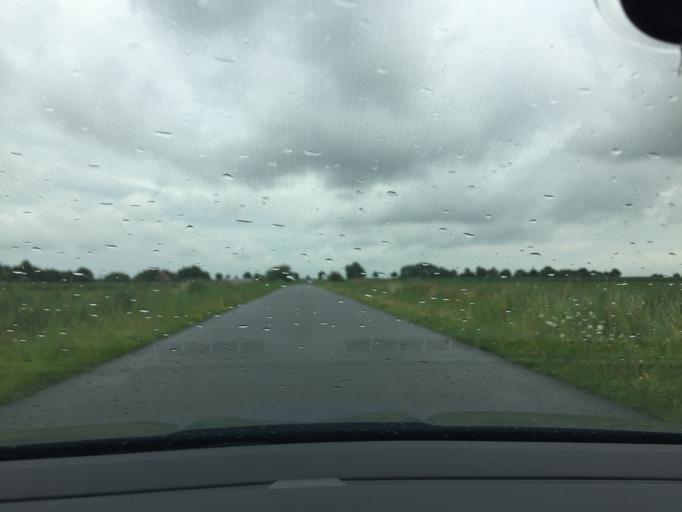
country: DE
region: Lower Saxony
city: Wirdum
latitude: 53.4970
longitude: 7.0614
